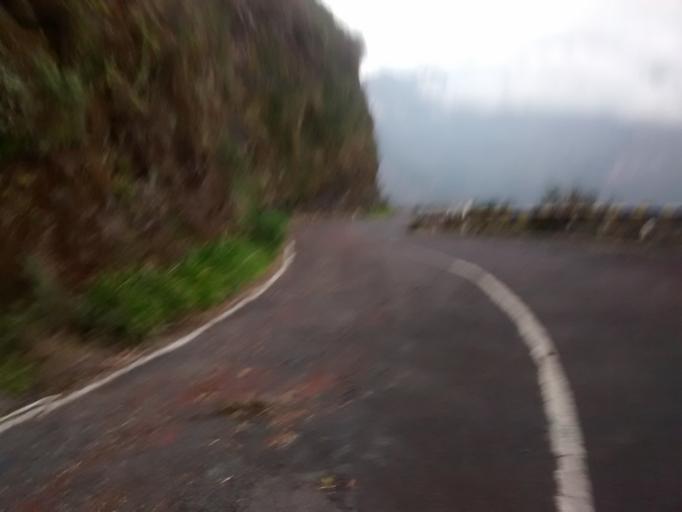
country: PT
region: Madeira
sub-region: Sao Vicente
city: Sao Vicente
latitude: 32.7460
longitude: -17.0411
